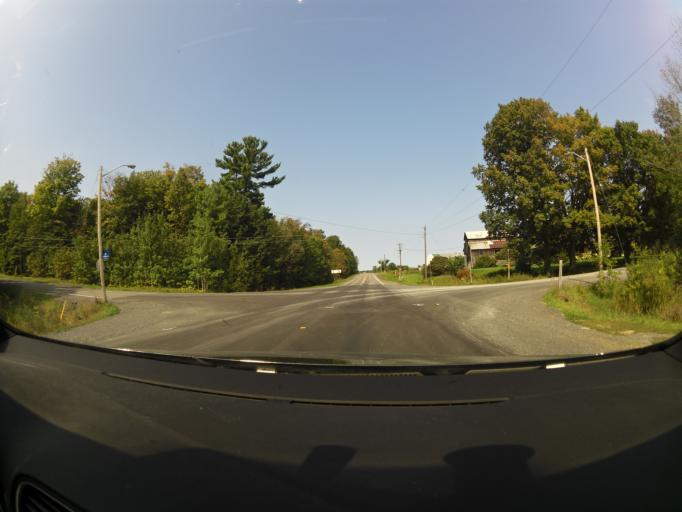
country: CA
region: Ontario
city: Arnprior
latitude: 45.4913
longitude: -76.1936
